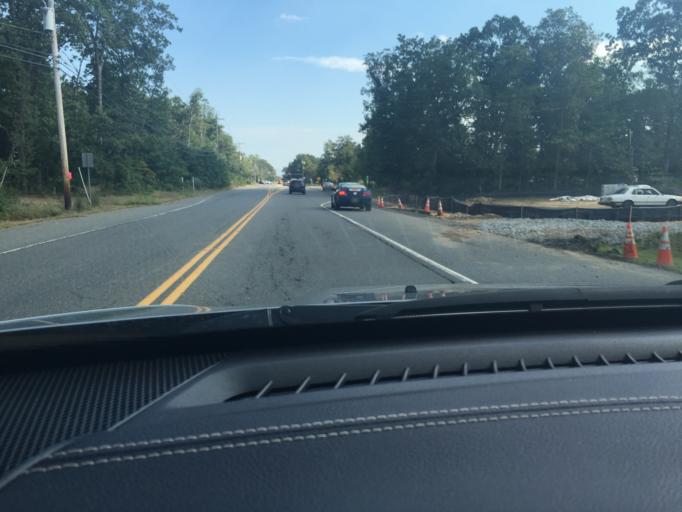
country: US
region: New Jersey
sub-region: Ocean County
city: Leisure Knoll
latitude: 40.0253
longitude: -74.2728
